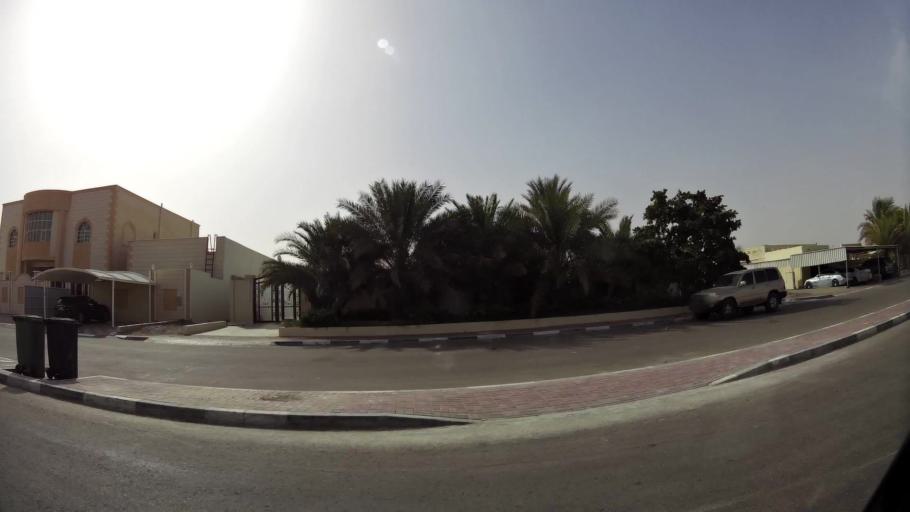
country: AE
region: Abu Dhabi
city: Al Ain
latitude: 24.2159
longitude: 55.5896
